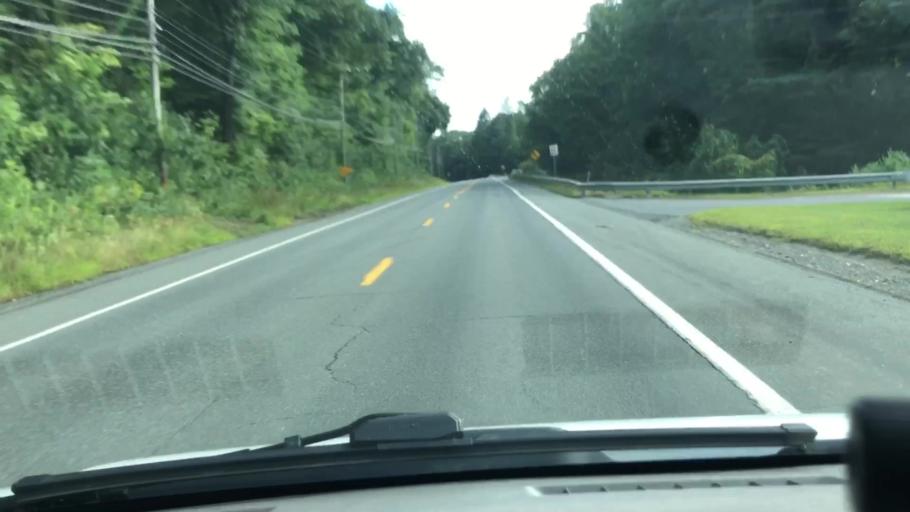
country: US
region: Massachusetts
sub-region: Franklin County
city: Shelburne Falls
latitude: 42.5972
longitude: -72.7286
